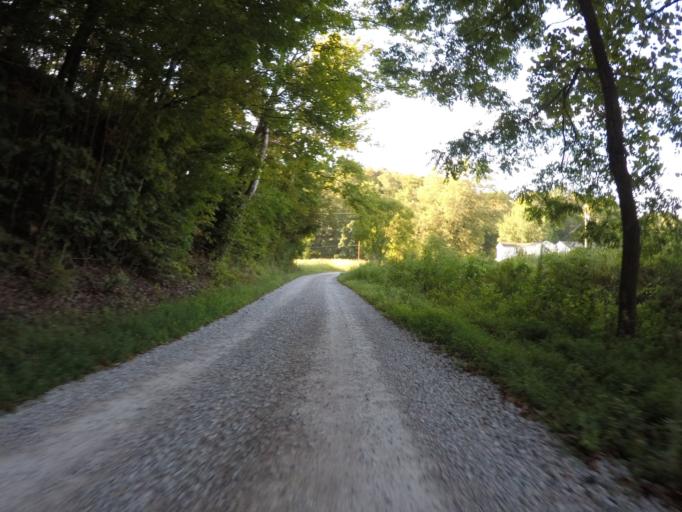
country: US
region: Ohio
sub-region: Lawrence County
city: Coal Grove
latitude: 38.5748
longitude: -82.5453
